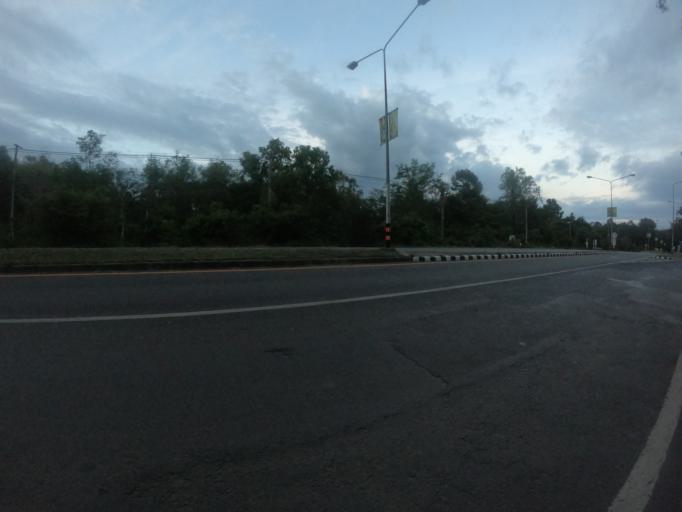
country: TH
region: Surin
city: Kap Choeng
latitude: 14.4514
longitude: 103.6978
